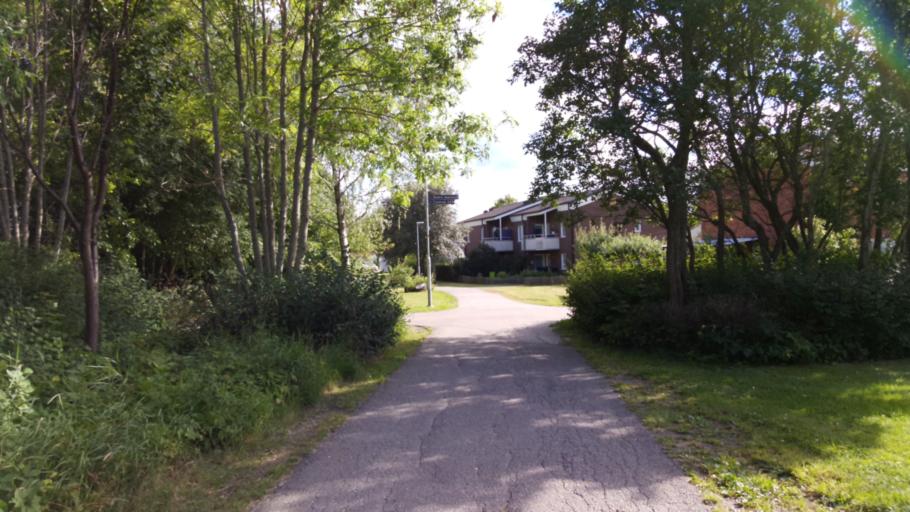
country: SE
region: Uppsala
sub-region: Uppsala Kommun
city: Gamla Uppsala
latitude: 59.8842
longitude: 17.6392
